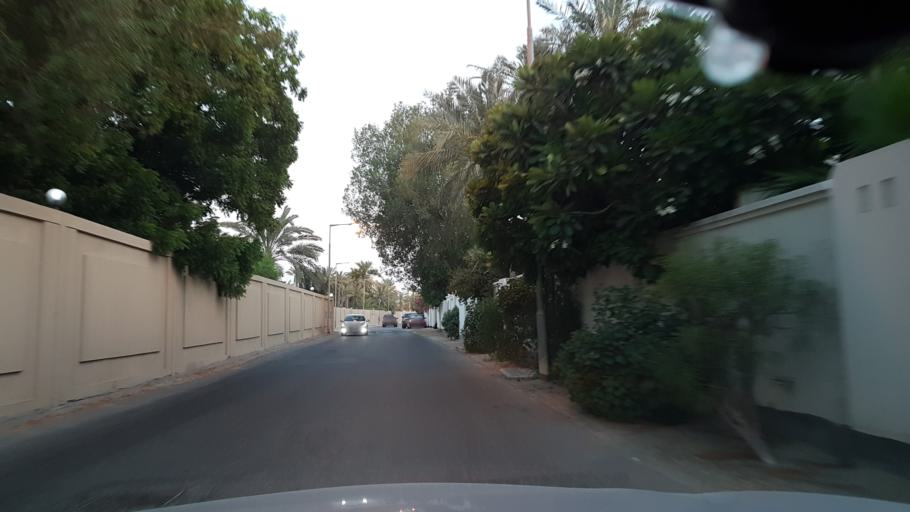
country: BH
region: Manama
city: Jidd Hafs
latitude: 26.2256
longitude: 50.4893
